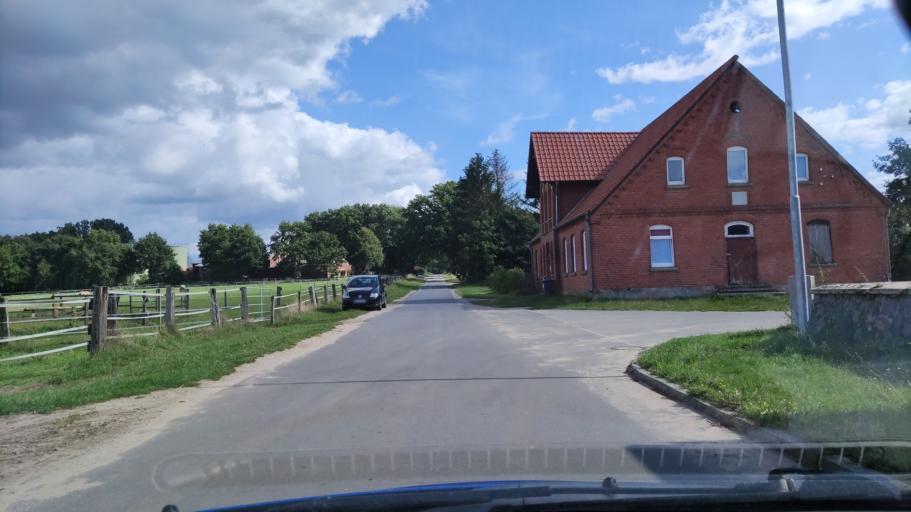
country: DE
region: Lower Saxony
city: Romstedt
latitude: 53.0808
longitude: 10.6422
